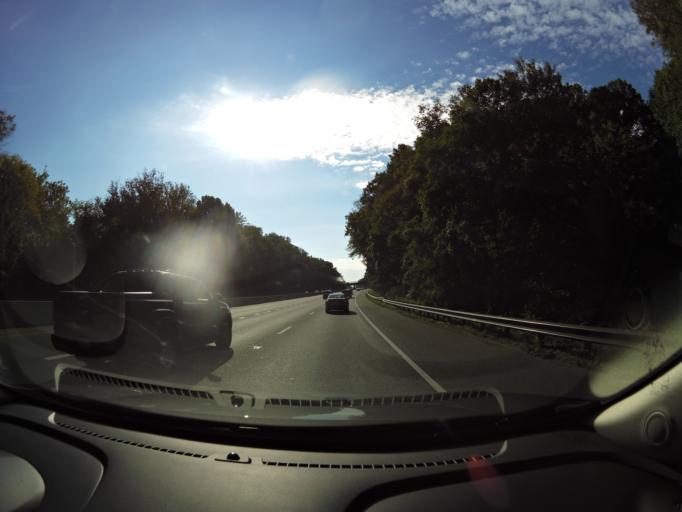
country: US
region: Maryland
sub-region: Montgomery County
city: North Bethesda
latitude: 39.0256
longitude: -77.1093
